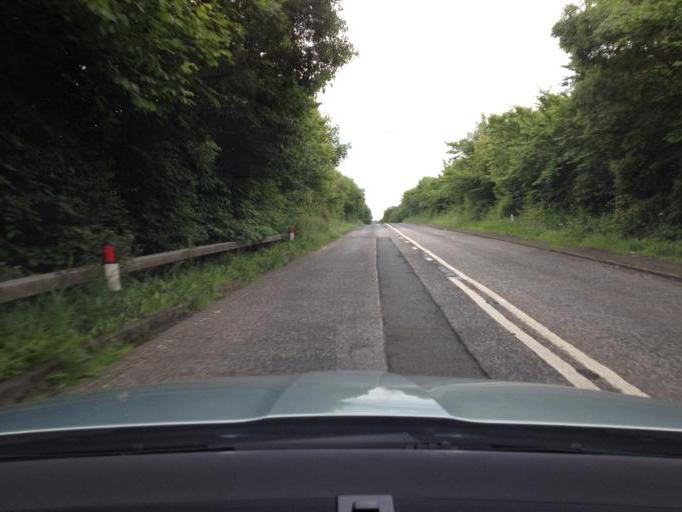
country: GB
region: Scotland
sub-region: West Lothian
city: West Calder
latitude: 55.8835
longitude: -3.5778
